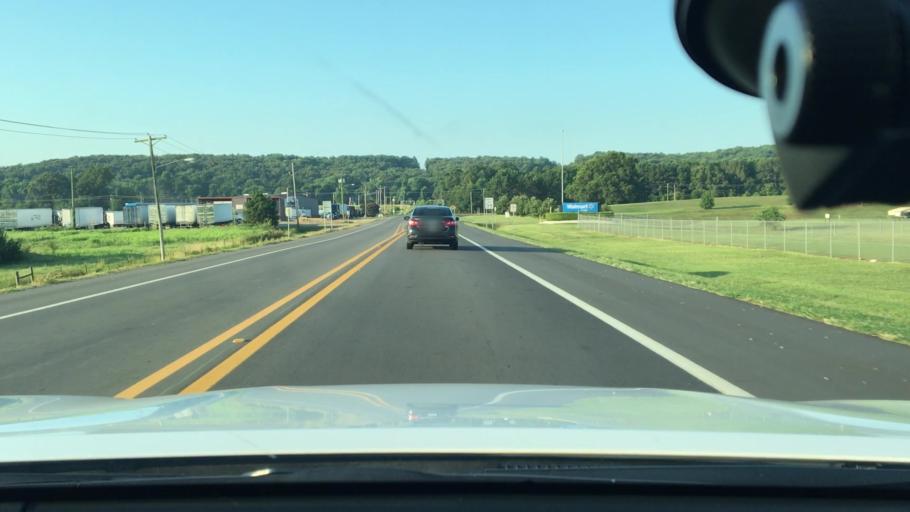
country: US
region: Arkansas
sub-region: Johnson County
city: Clarksville
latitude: 35.4296
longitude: -93.5295
